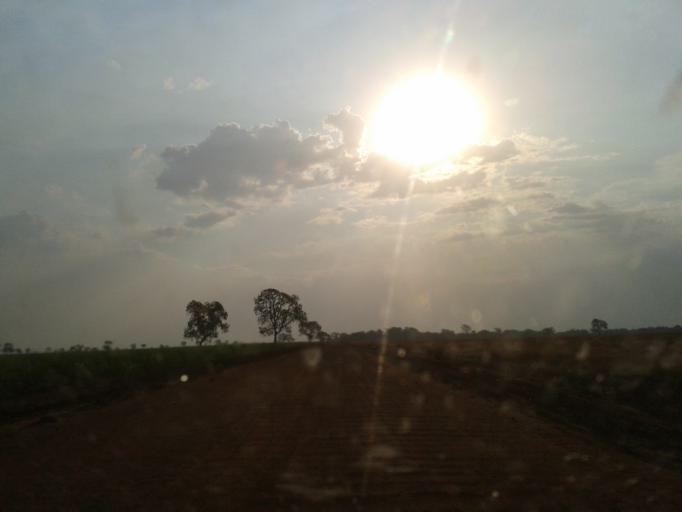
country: BR
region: Minas Gerais
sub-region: Capinopolis
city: Capinopolis
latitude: -18.7563
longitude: -49.7011
